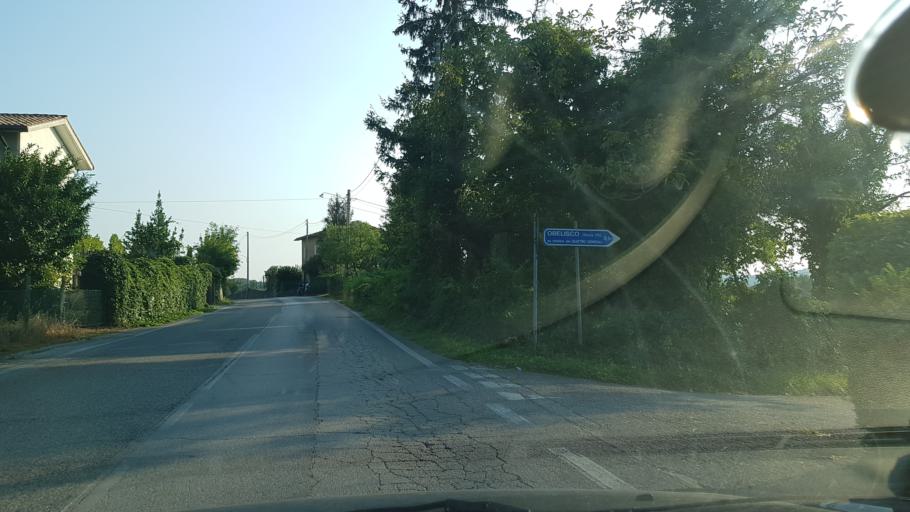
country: IT
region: Friuli Venezia Giulia
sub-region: Provincia di Gorizia
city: San Floriano del Collio
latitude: 45.9758
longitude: 13.6118
